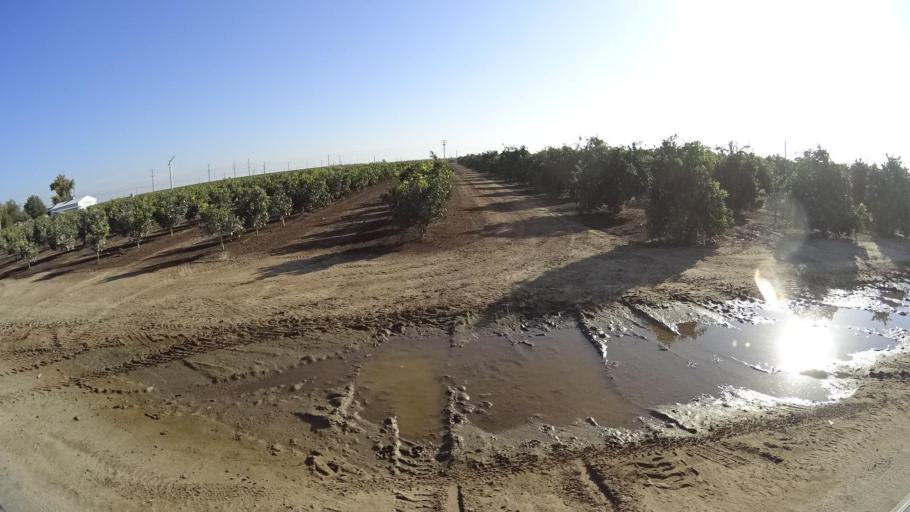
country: US
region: California
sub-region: Tulare County
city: Richgrove
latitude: 35.7741
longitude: -119.1607
